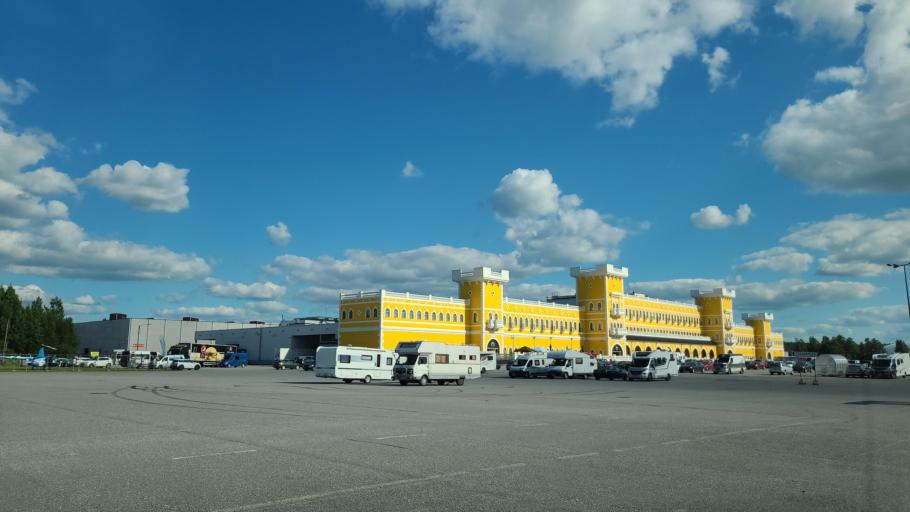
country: FI
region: Southern Ostrobothnia
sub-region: Kuusiokunnat
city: Toeysae
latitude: 62.6051
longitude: 23.7208
